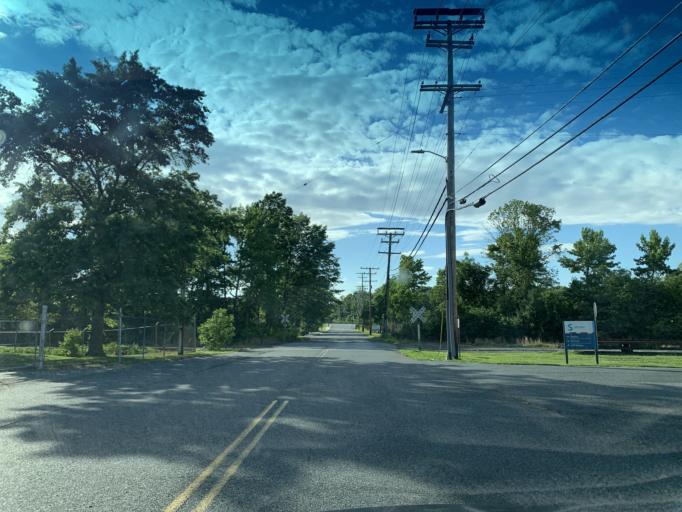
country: US
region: Maryland
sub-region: Harford County
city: Havre de Grace
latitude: 39.5353
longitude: -76.1099
